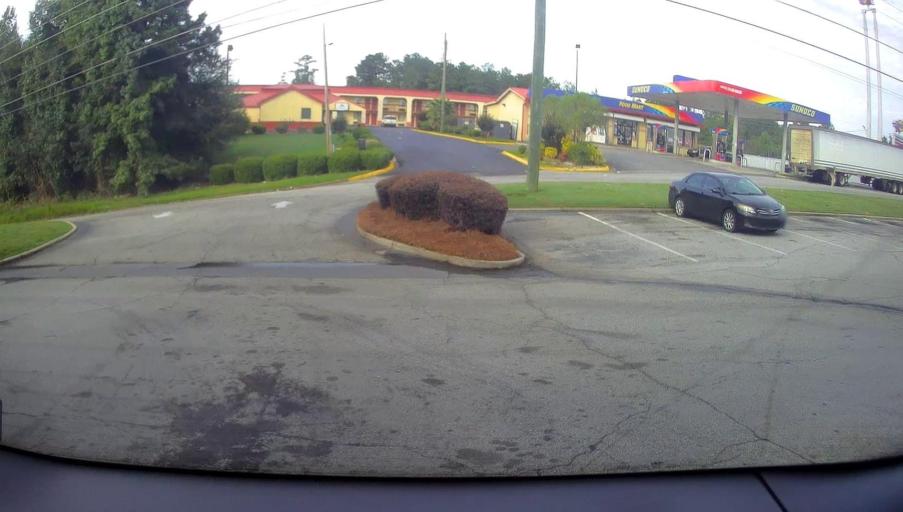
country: US
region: Georgia
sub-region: Bibb County
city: West Point
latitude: 32.8076
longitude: -83.7277
